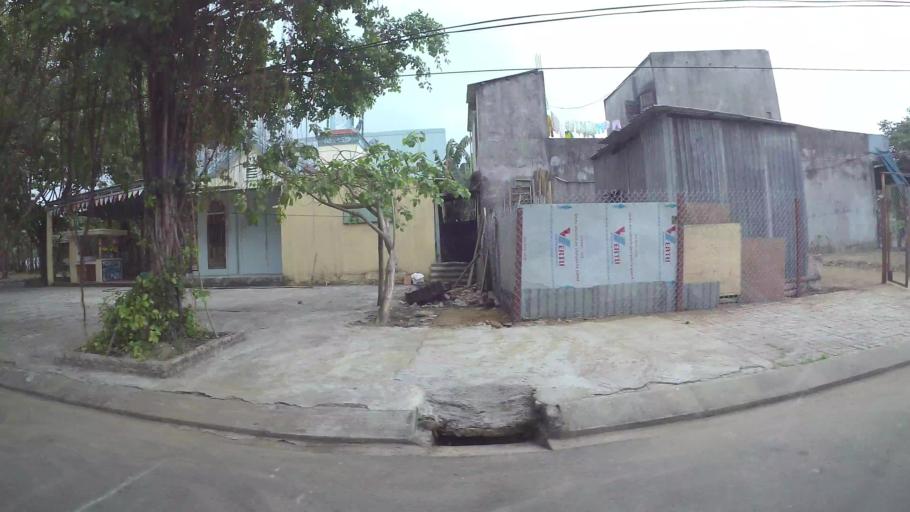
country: VN
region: Da Nang
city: Lien Chieu
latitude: 16.0744
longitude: 108.1656
